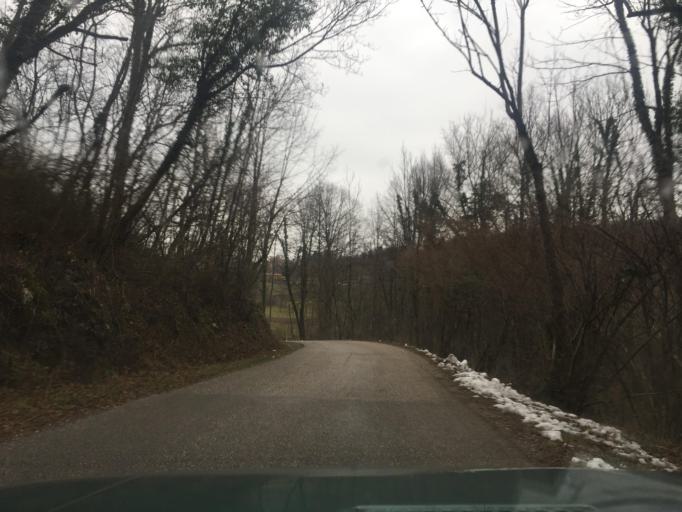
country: SI
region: Kanal
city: Kanal
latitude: 46.0712
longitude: 13.6655
